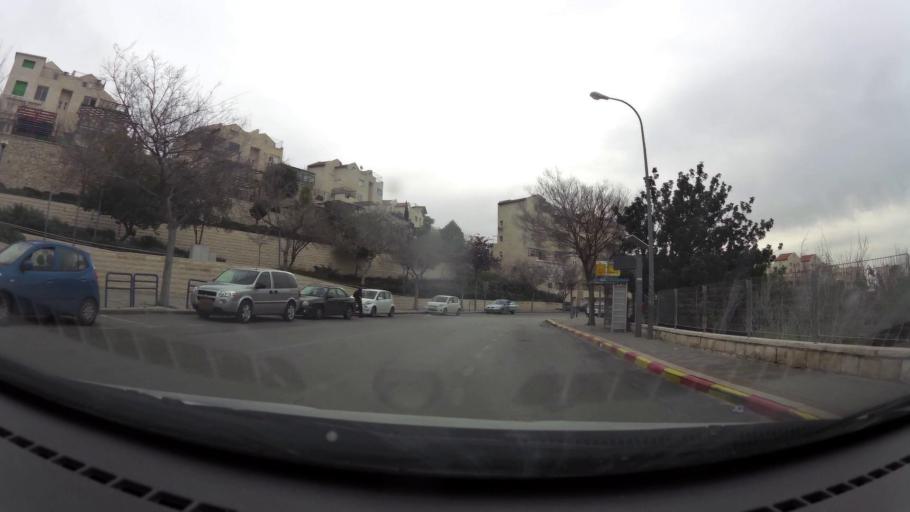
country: IL
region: Jerusalem
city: Bet Shemesh
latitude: 31.7118
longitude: 34.9968
